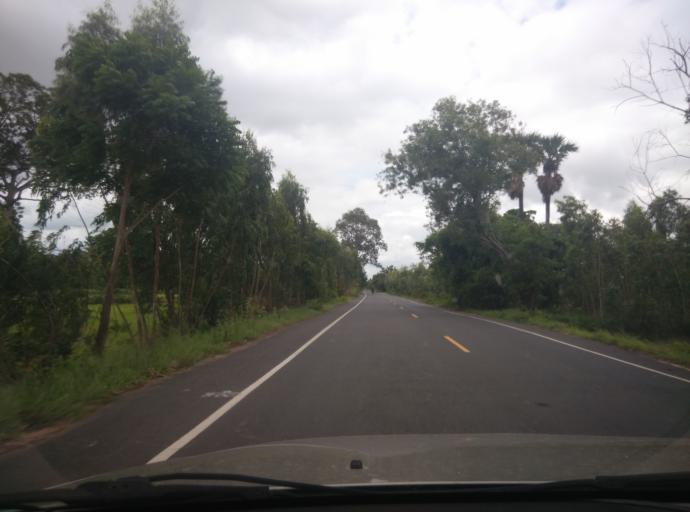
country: TH
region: Sisaket
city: Uthumphon Phisai
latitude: 15.1313
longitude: 104.1533
